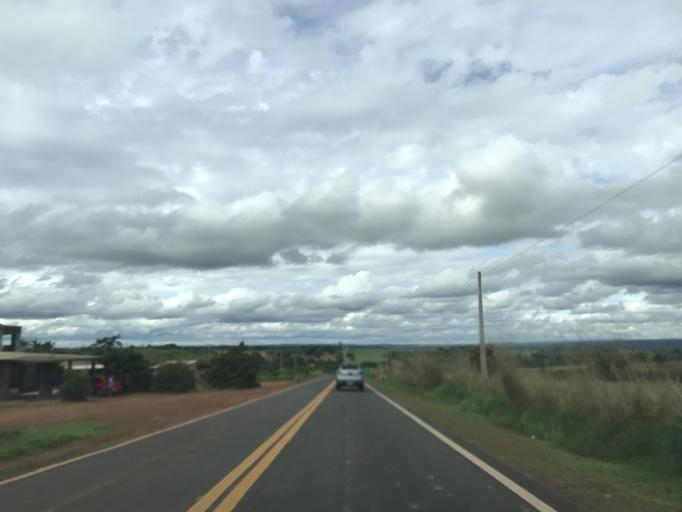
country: BR
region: Goias
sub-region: Piracanjuba
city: Piracanjuba
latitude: -17.2013
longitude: -48.7023
